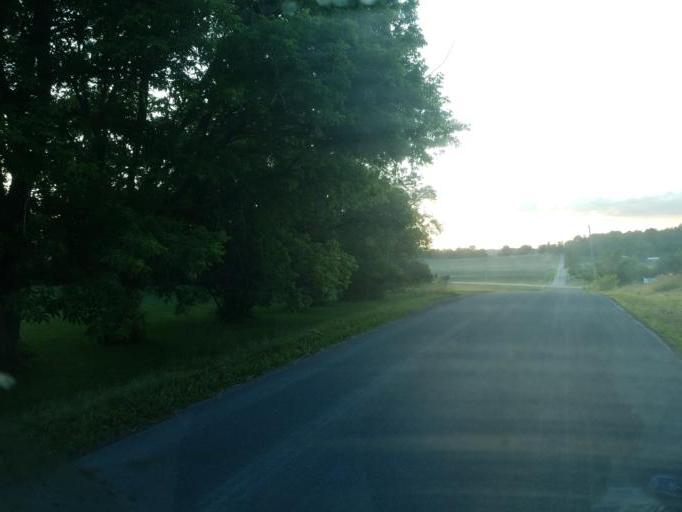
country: US
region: New York
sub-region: Wayne County
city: Clyde
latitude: 43.0448
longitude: -76.9036
